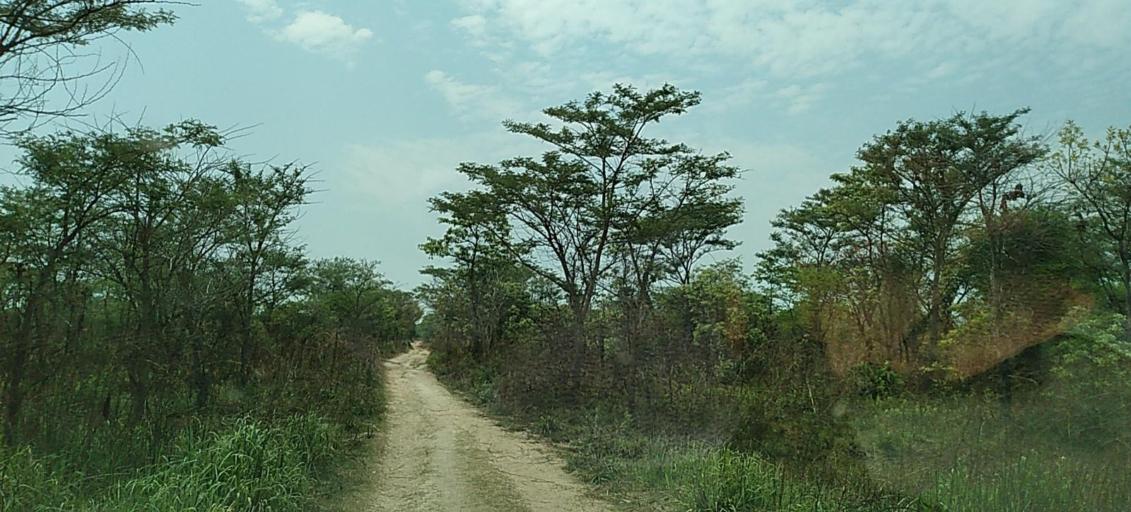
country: ZM
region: Copperbelt
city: Kalulushi
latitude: -12.9471
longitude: 28.1294
